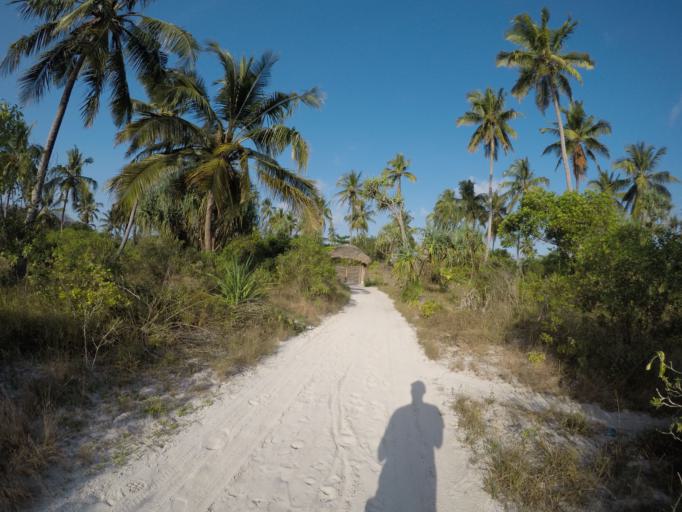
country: TZ
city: Kiwengwa
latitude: -6.1419
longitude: 39.4920
